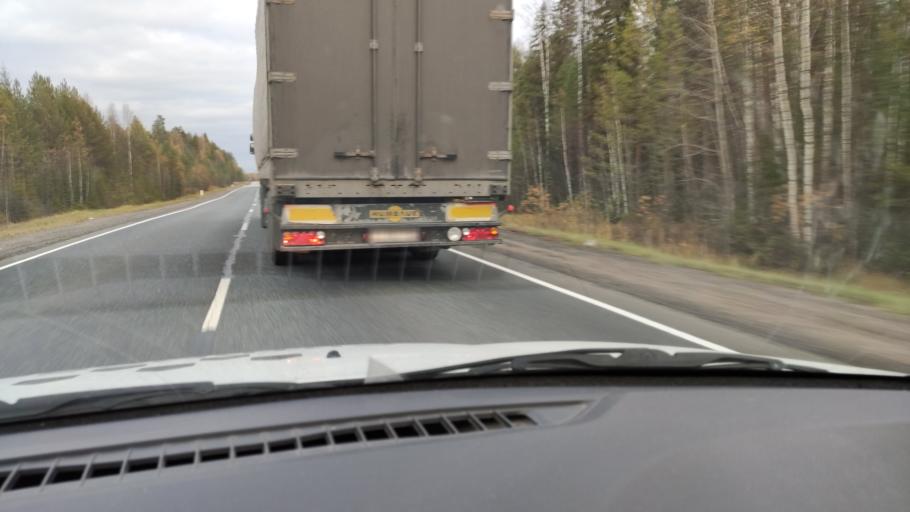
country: RU
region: Kirov
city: Dubrovka
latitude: 58.9070
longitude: 51.2314
